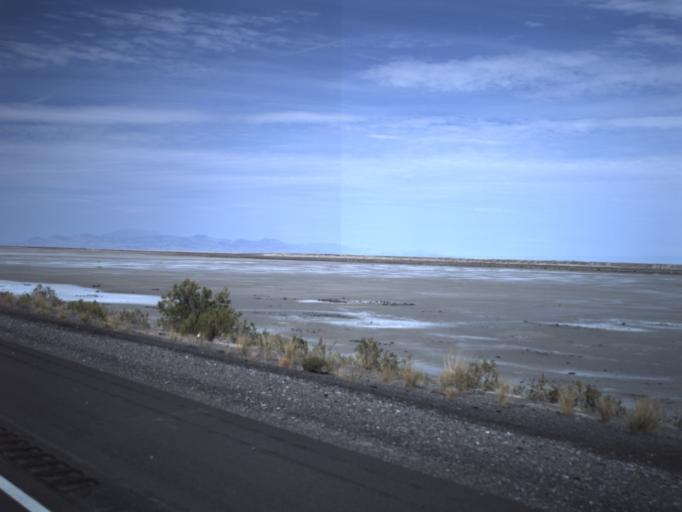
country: US
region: Utah
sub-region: Tooele County
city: Wendover
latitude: 40.7280
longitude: -113.2949
